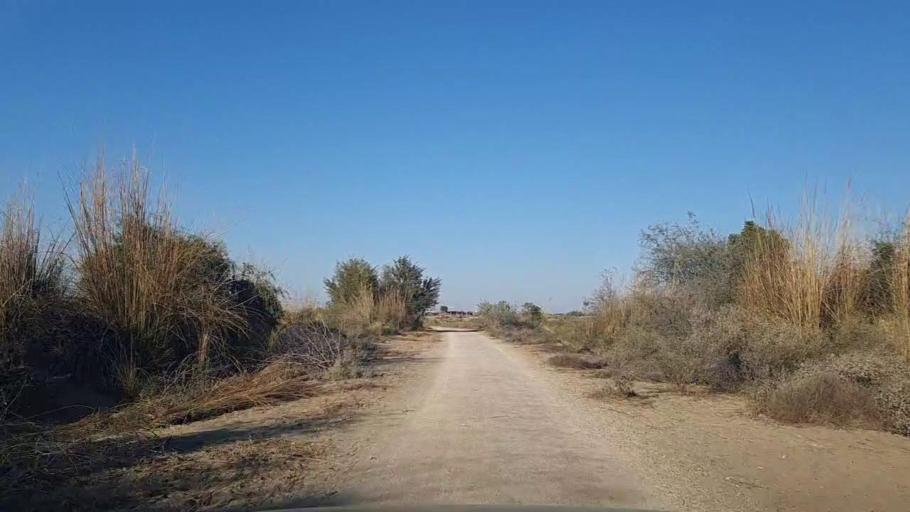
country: PK
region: Sindh
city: Khadro
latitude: 26.2541
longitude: 68.8673
